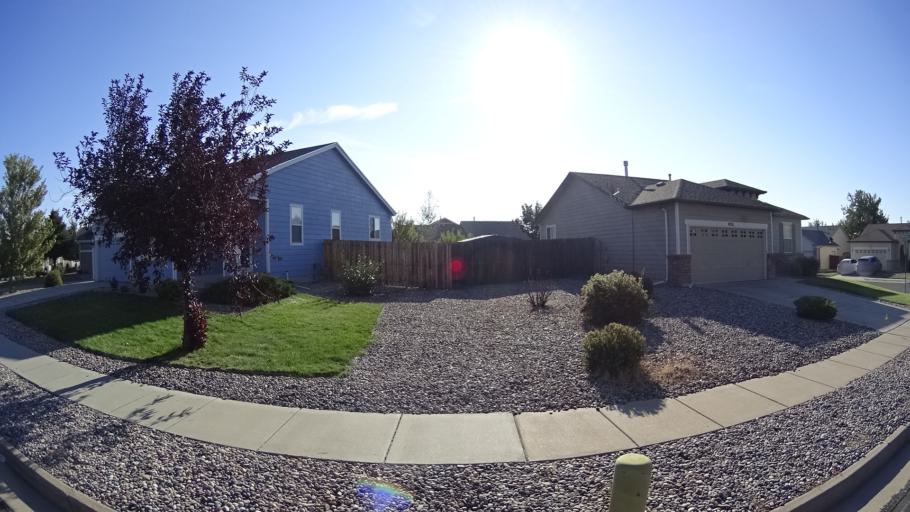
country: US
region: Colorado
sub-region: El Paso County
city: Cimarron Hills
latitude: 38.8918
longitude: -104.6936
